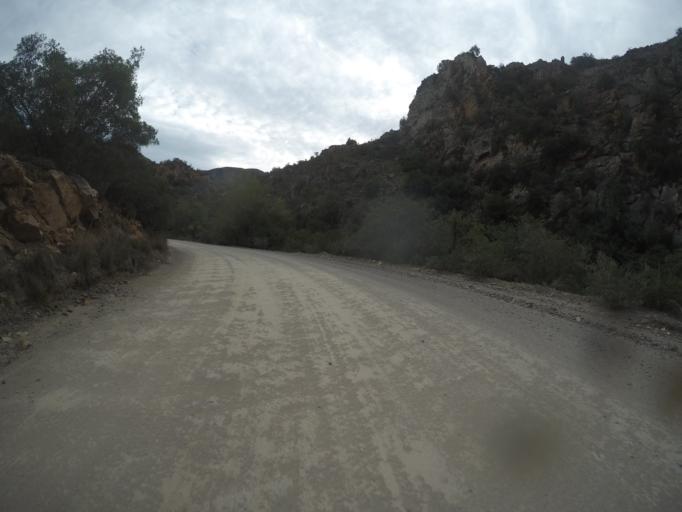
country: ZA
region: Eastern Cape
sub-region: Cacadu District Municipality
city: Willowmore
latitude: -33.5093
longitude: 23.6388
